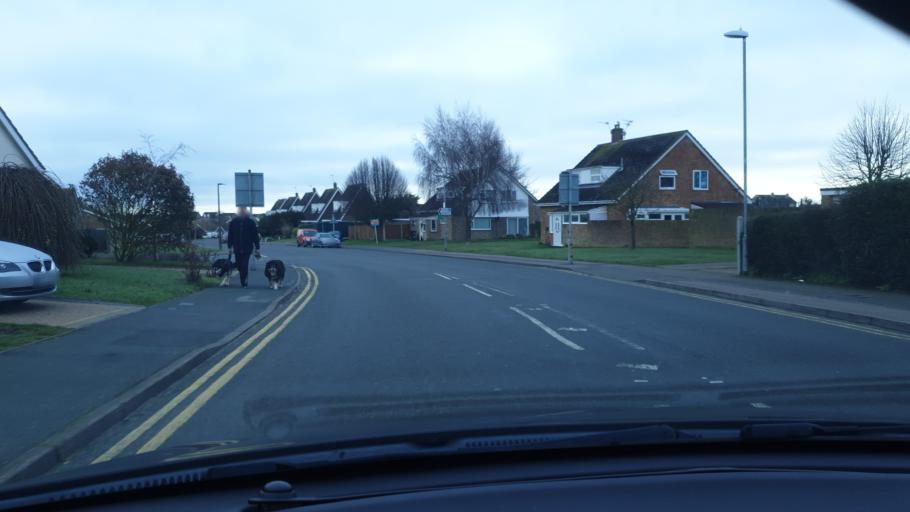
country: GB
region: England
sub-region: Essex
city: Frinton-on-Sea
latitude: 51.8436
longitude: 1.2505
